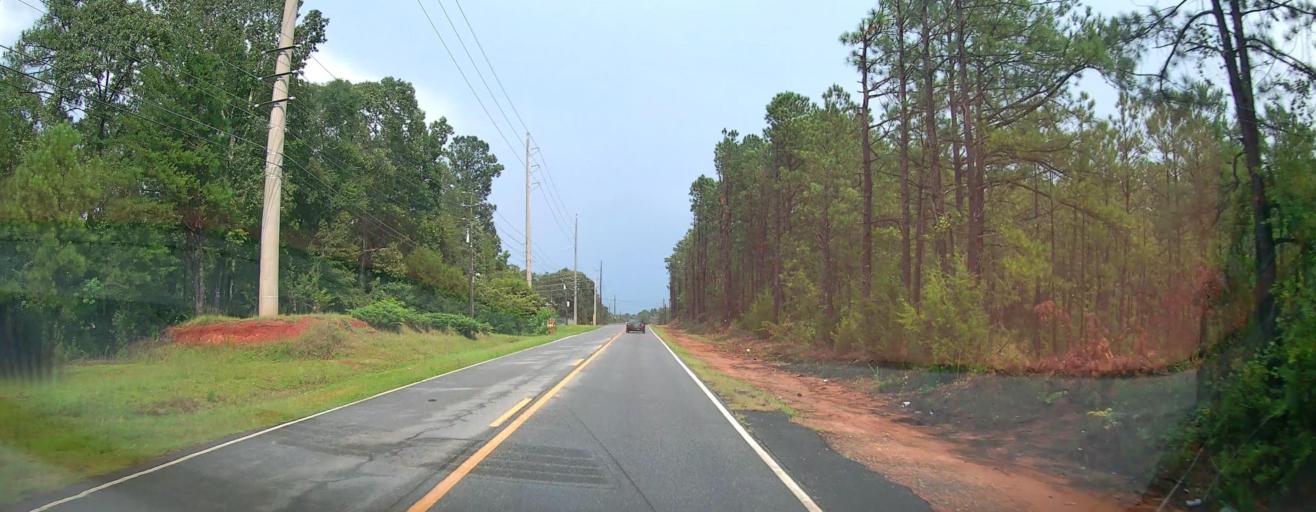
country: US
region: Georgia
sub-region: Houston County
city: Warner Robins
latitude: 32.6509
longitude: -83.6327
